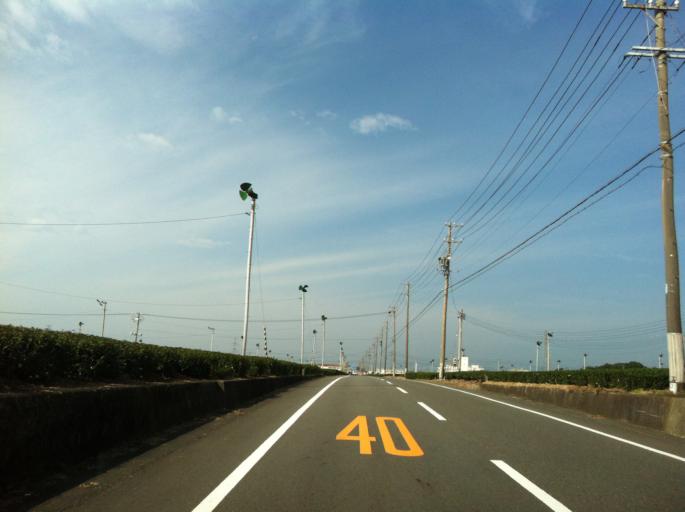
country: JP
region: Shizuoka
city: Shimada
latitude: 34.7726
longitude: 138.1535
